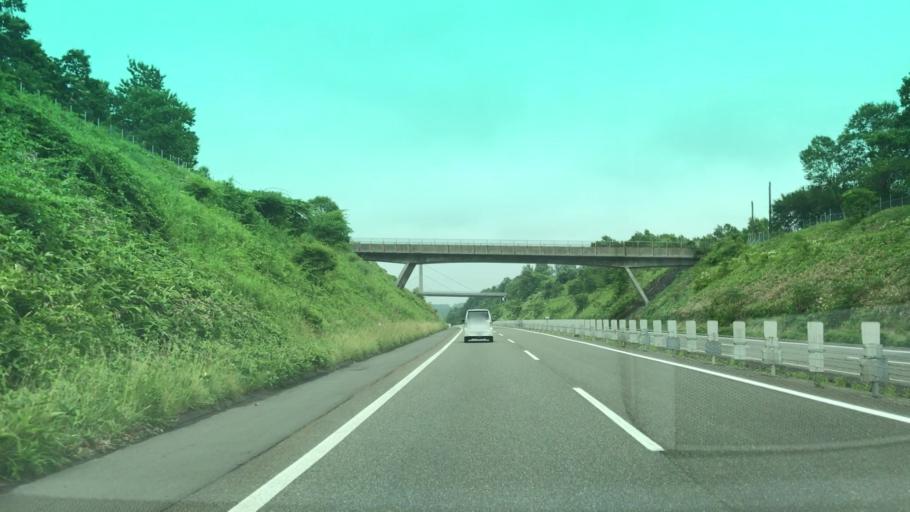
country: JP
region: Hokkaido
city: Tomakomai
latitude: 42.6208
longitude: 141.4772
